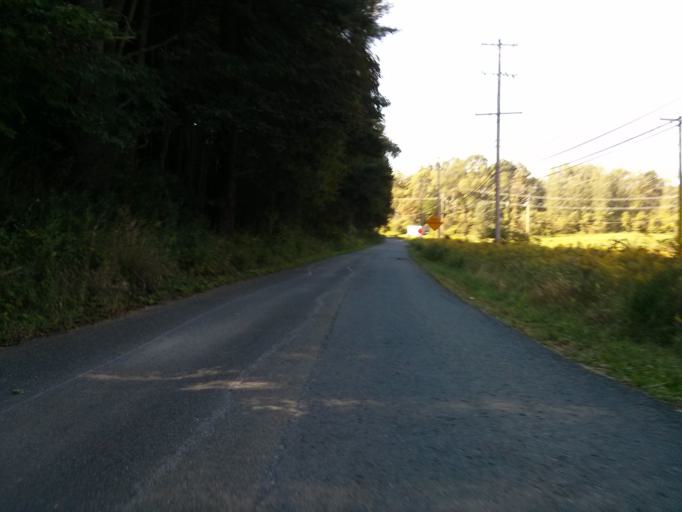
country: US
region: Pennsylvania
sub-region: Centre County
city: State College
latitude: 40.8175
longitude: -77.8742
